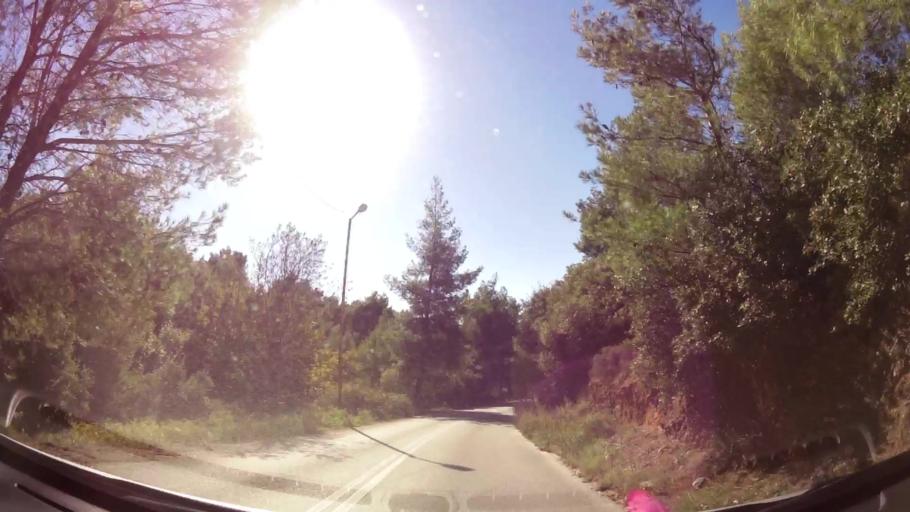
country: GR
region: Attica
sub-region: Nomarchia Anatolikis Attikis
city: Varybobi
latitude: 38.1325
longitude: 23.7871
